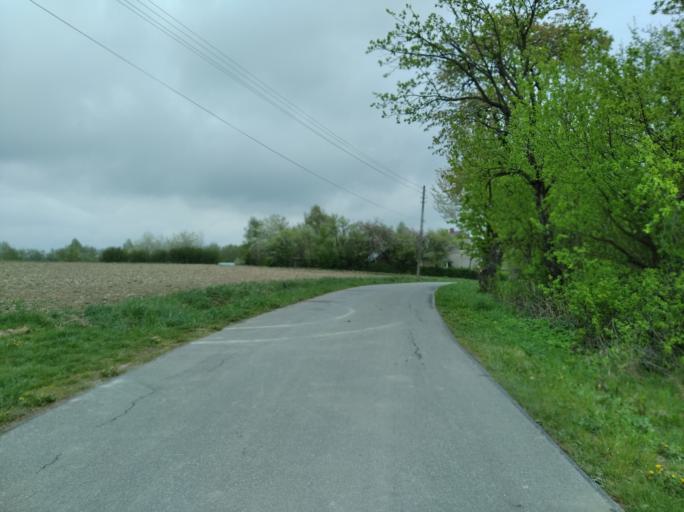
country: PL
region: Subcarpathian Voivodeship
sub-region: Powiat brzozowski
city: Golcowa
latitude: 49.7533
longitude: 22.0398
